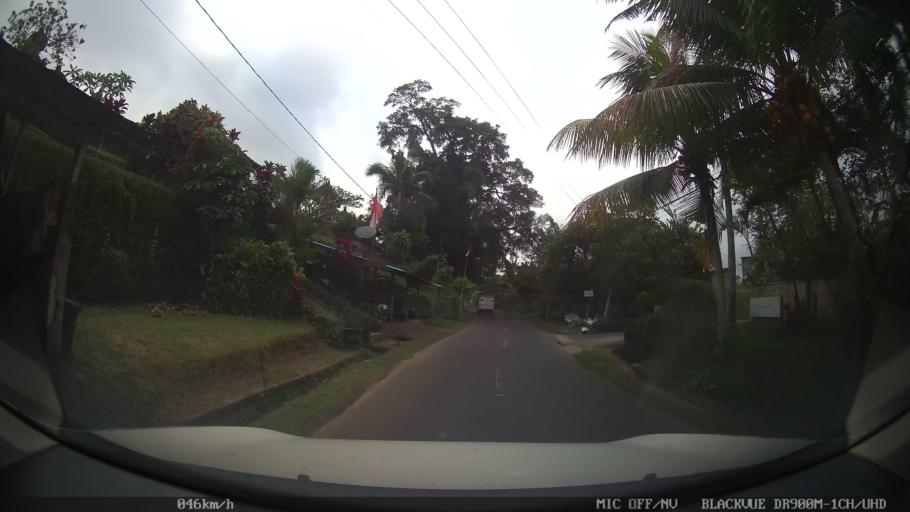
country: ID
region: Bali
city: Bunutan
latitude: -8.4706
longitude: 115.2600
